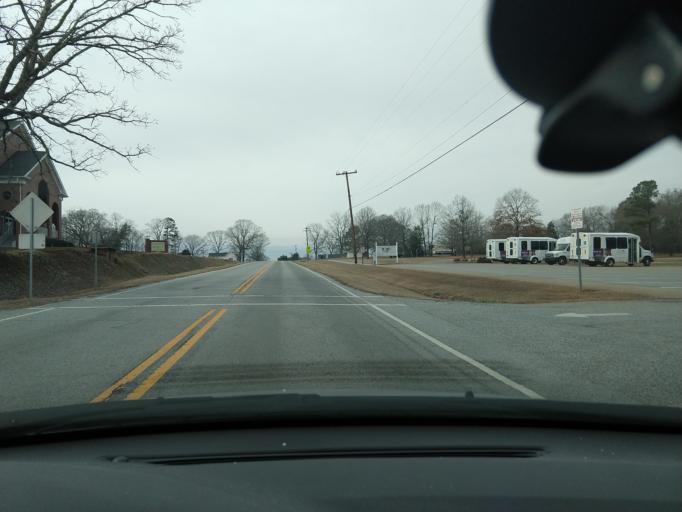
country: US
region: South Carolina
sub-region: Spartanburg County
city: Cowpens
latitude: 35.0091
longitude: -81.8593
